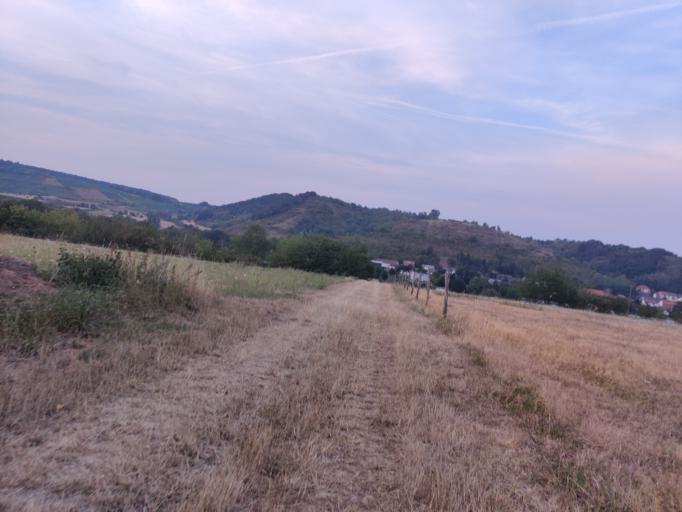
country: DE
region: Rheinland-Pfalz
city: Gutenberg
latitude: 49.8790
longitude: 7.7897
